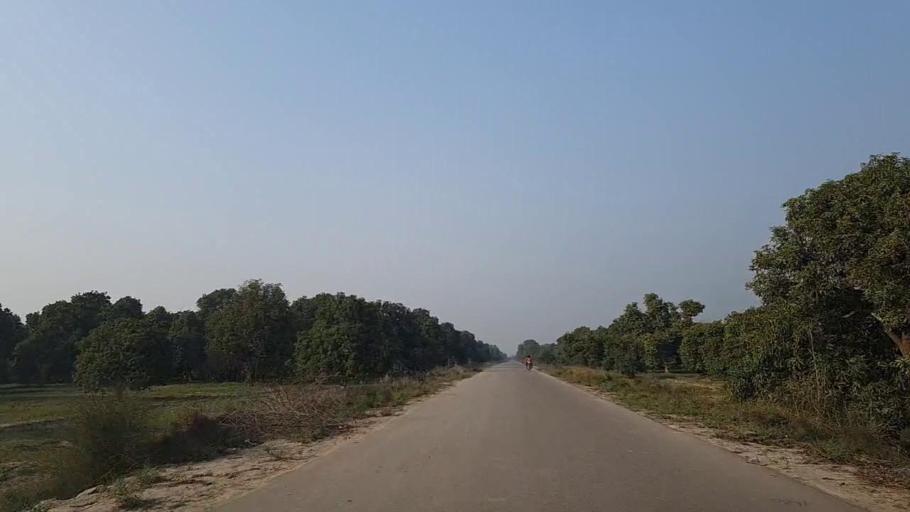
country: PK
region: Sindh
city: Sann
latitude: 26.1023
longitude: 68.1518
